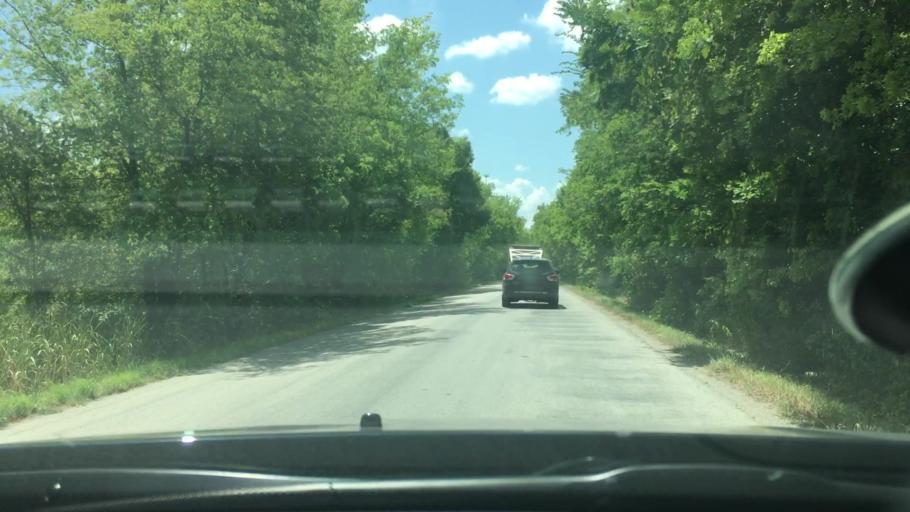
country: US
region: Oklahoma
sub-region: Carter County
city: Ardmore
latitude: 34.0746
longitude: -97.1516
